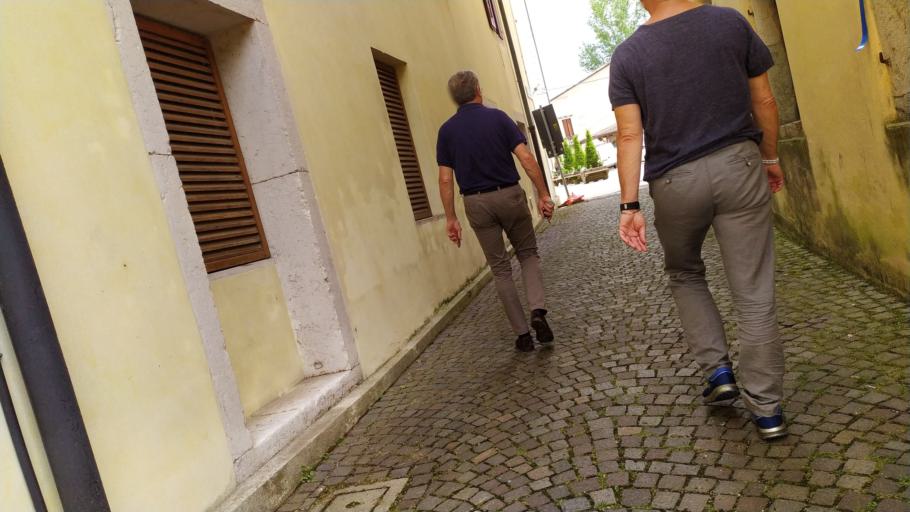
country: IT
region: Friuli Venezia Giulia
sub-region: Provincia di Pordenone
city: Polcenigo
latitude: 46.0305
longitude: 12.5013
